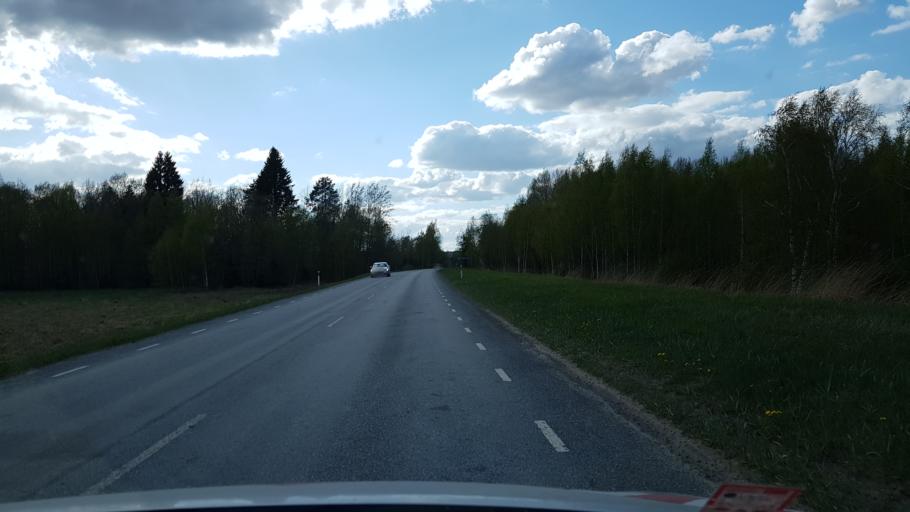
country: EE
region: Tartu
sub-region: UElenurme vald
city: Ulenurme
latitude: 58.3281
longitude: 26.7487
